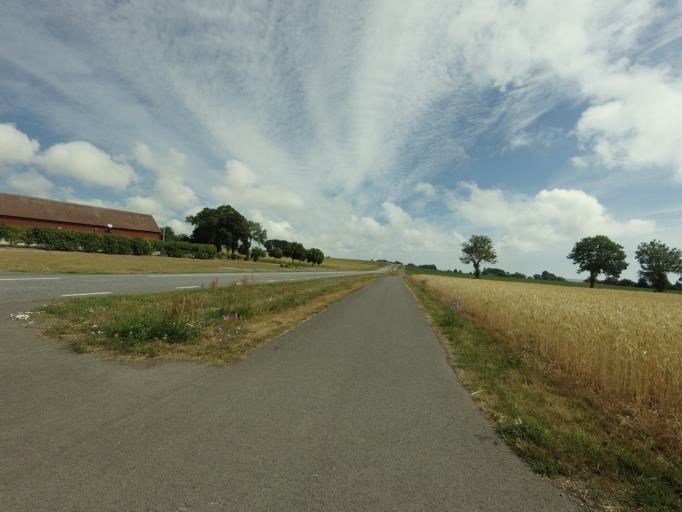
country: SE
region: Skane
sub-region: Simrishamns Kommun
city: Simrishamn
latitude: 55.4901
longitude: 14.3080
